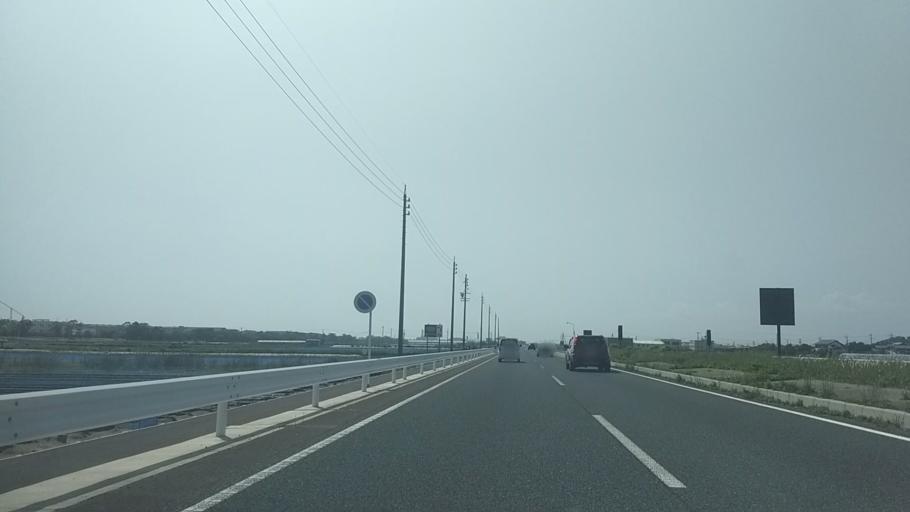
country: JP
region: Shizuoka
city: Hamamatsu
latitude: 34.6733
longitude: 137.6980
